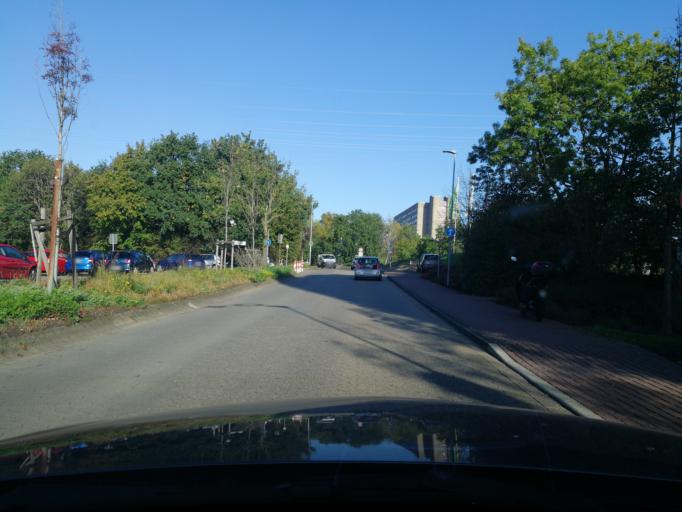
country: DE
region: North Rhine-Westphalia
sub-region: Regierungsbezirk Dusseldorf
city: Dusseldorf
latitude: 51.1919
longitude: 6.7921
